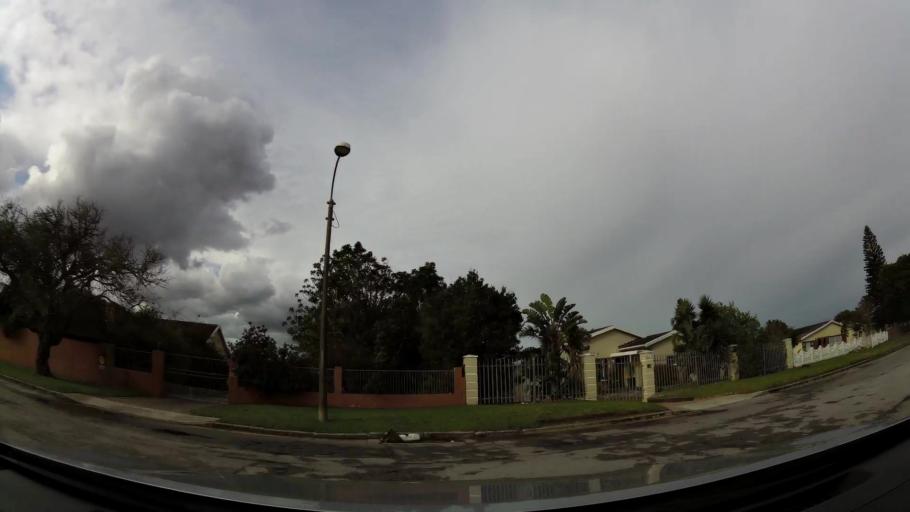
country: ZA
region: Eastern Cape
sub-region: Nelson Mandela Bay Metropolitan Municipality
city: Port Elizabeth
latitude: -33.9365
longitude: 25.4980
